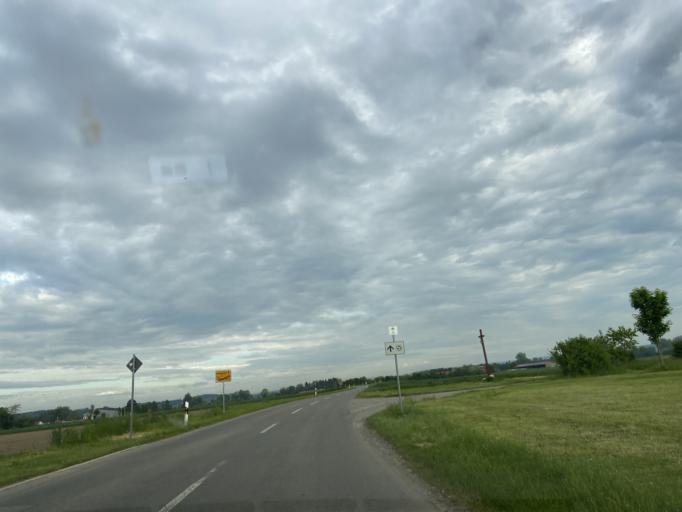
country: DE
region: Baden-Wuerttemberg
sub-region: Tuebingen Region
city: Hohentengen
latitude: 48.0375
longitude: 9.3844
